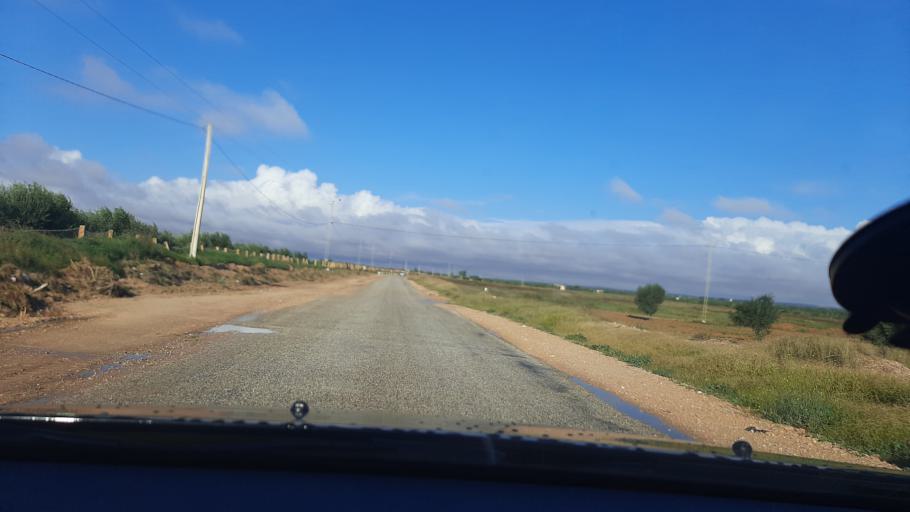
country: TN
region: Safaqis
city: Sfax
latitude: 34.8874
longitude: 10.6246
